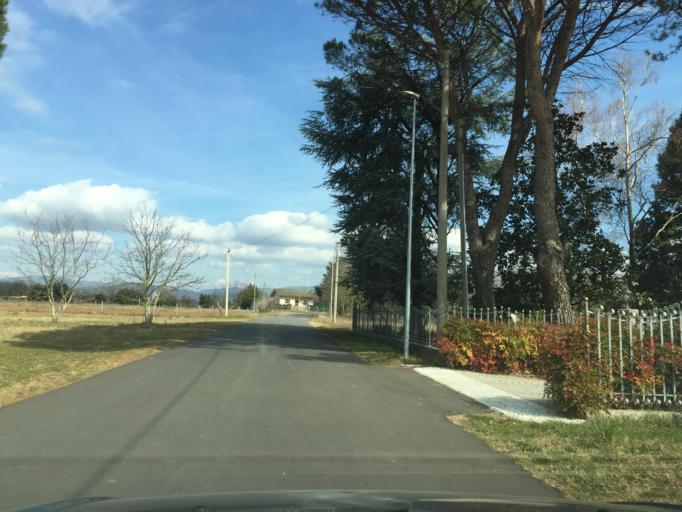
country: IT
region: Friuli Venezia Giulia
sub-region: Provincia di Gorizia
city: Savogna d'Isonzo
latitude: 45.8978
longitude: 13.5912
